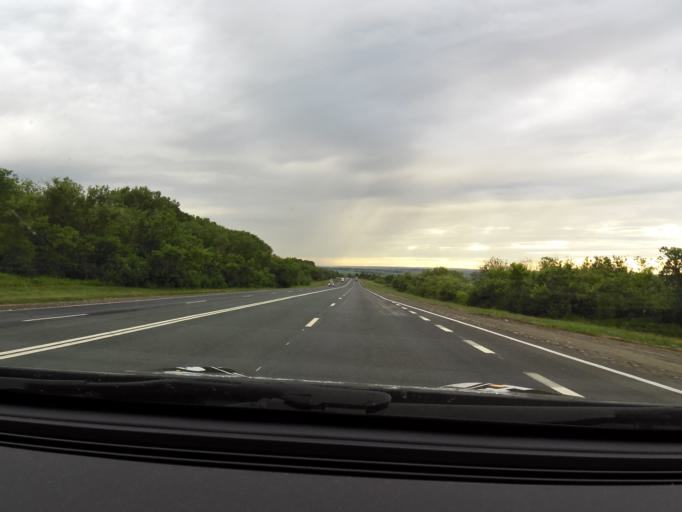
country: RU
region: Chuvashia
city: Yantikovo
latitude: 55.8102
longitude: 48.0178
